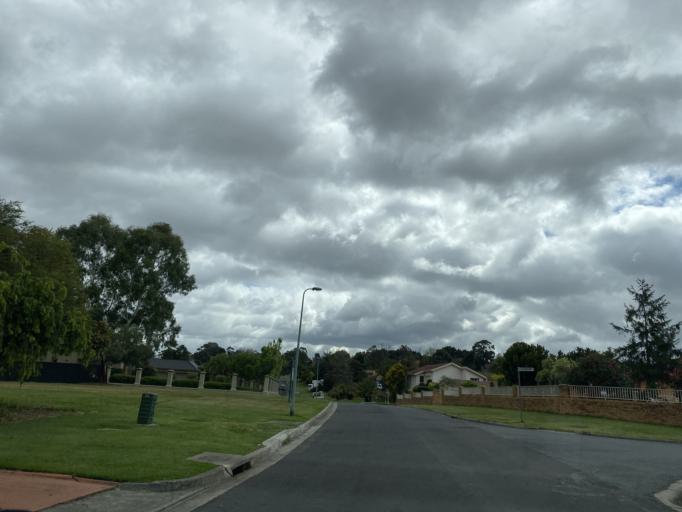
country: AU
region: Victoria
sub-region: Nillumbik
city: Eltham
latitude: -37.7521
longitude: 145.1395
